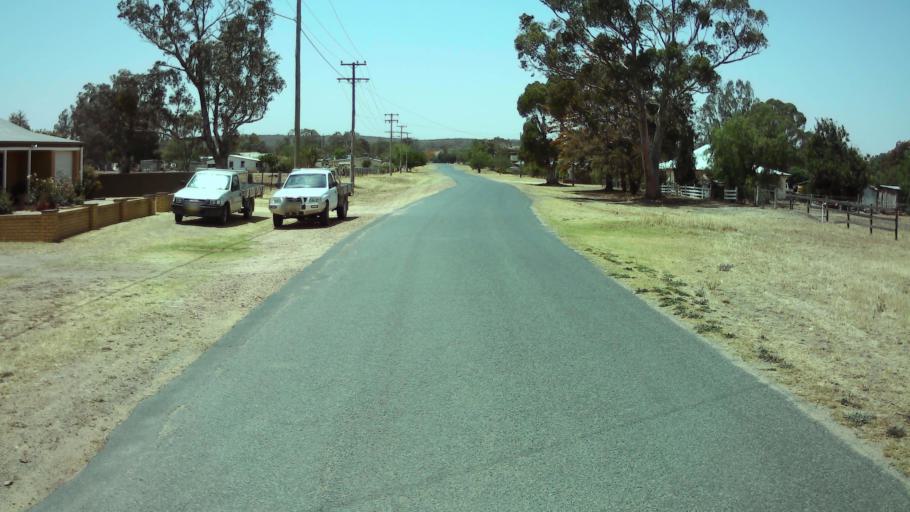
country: AU
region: New South Wales
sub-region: Weddin
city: Grenfell
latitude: -33.8895
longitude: 148.1545
